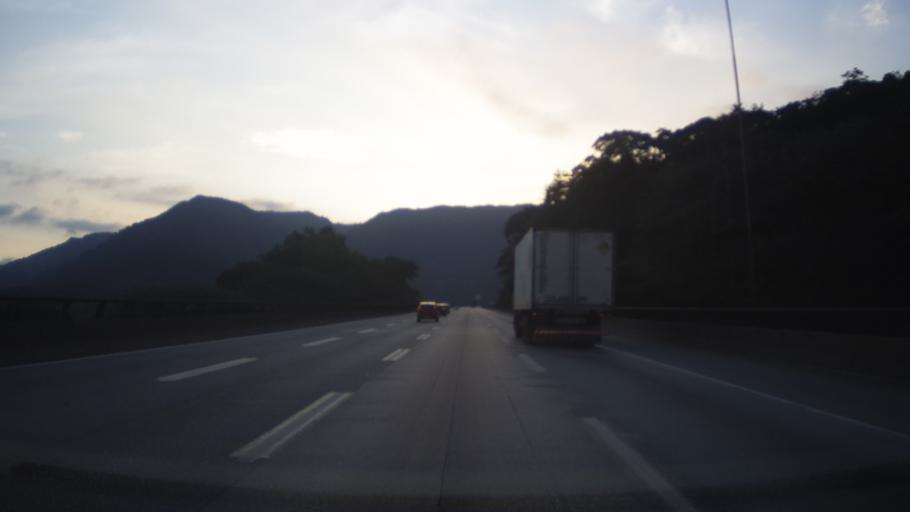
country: BR
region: Sao Paulo
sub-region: Cubatao
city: Cubatao
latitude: -23.8992
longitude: -46.4841
